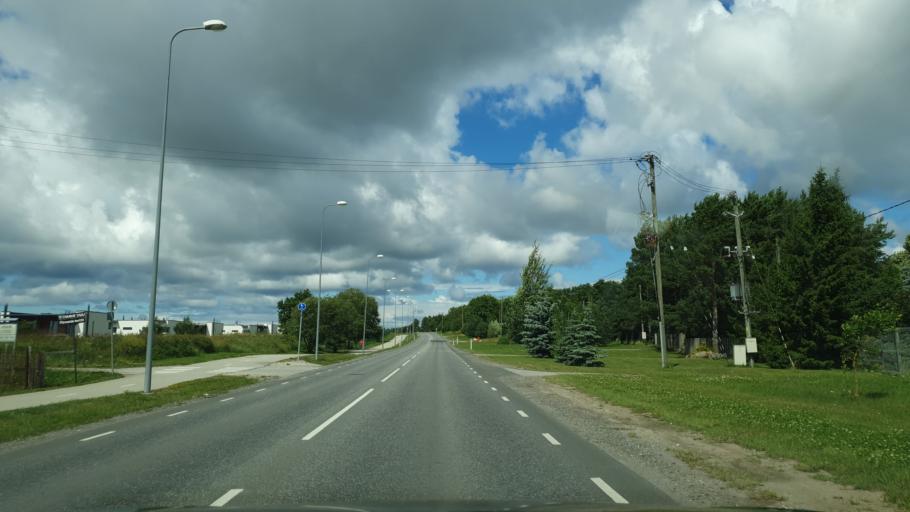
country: EE
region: Harju
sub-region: Viimsi vald
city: Viimsi
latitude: 59.4972
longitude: 24.8734
